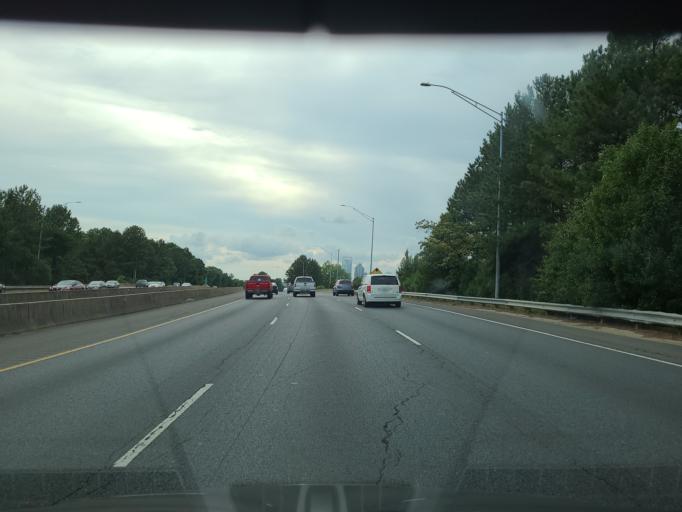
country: US
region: North Carolina
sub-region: Mecklenburg County
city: Charlotte
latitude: 35.2180
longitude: -80.8133
